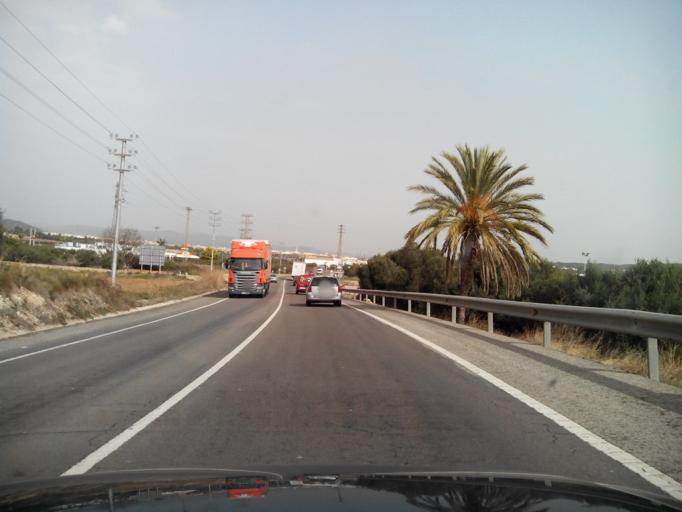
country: ES
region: Catalonia
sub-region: Provincia de Tarragona
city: El Vendrell
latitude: 41.1971
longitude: 1.5278
